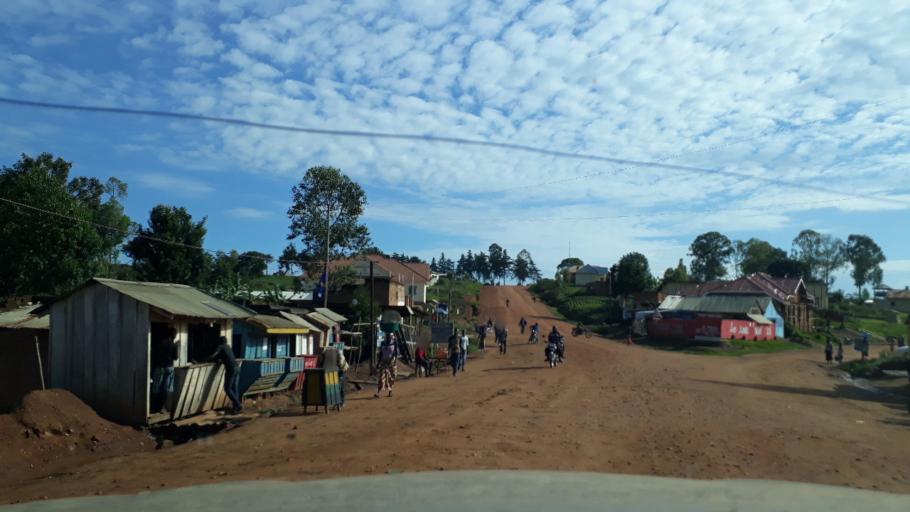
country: UG
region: Northern Region
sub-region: Zombo District
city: Paidha
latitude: 2.3015
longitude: 30.9931
